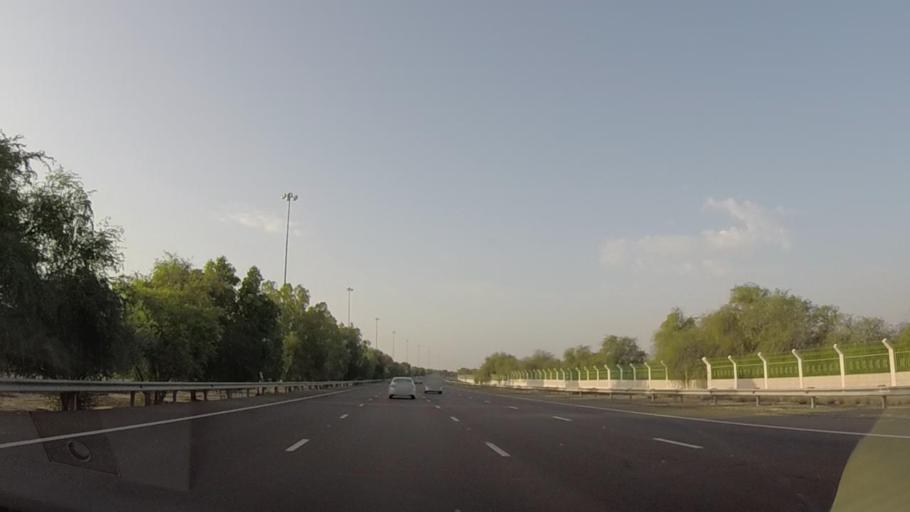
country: AE
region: Dubai
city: Dubai
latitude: 24.7718
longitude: 54.8498
